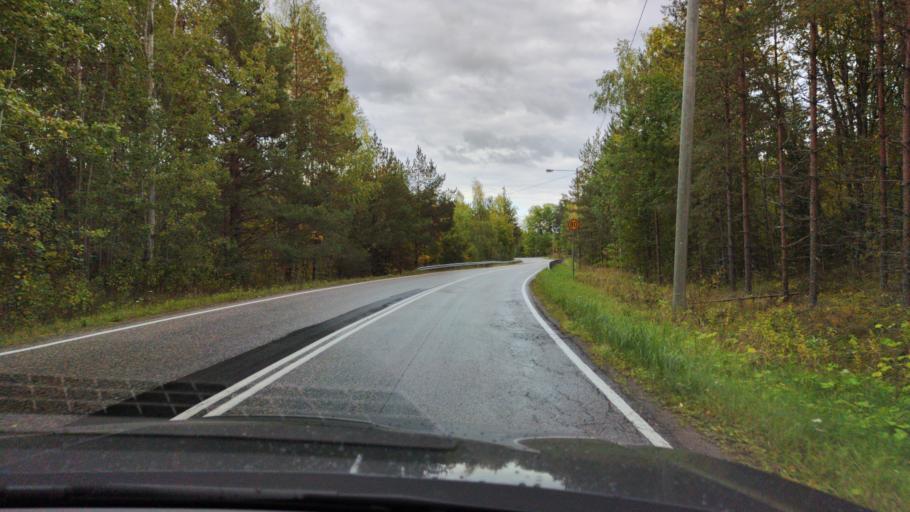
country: FI
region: Varsinais-Suomi
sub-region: Turku
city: Turku
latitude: 60.3670
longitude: 22.2223
